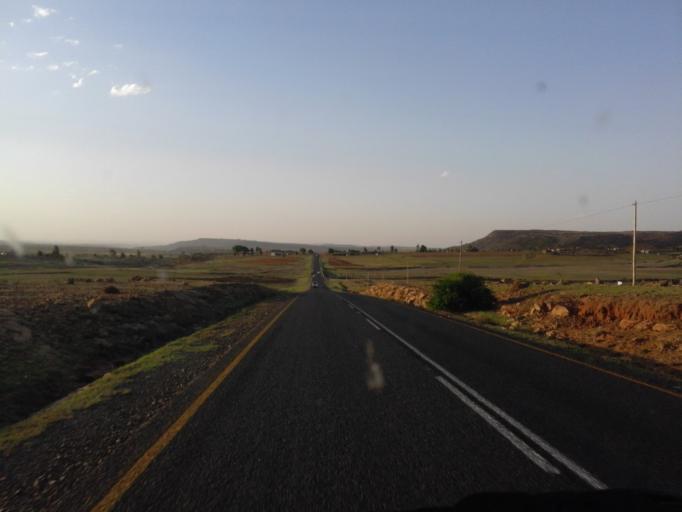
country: LS
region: Mafeteng
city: Mafeteng
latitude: -29.8897
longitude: 27.2527
